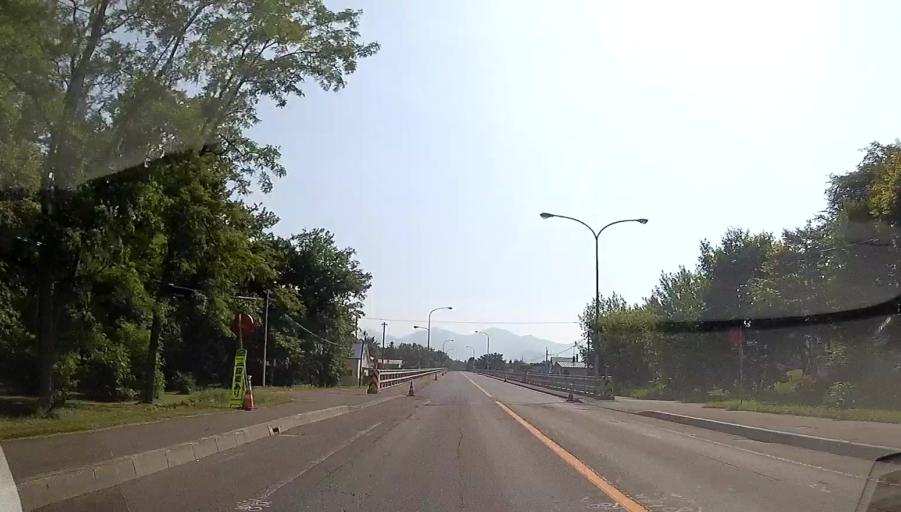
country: JP
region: Hokkaido
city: Otofuke
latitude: 43.0105
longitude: 142.8841
